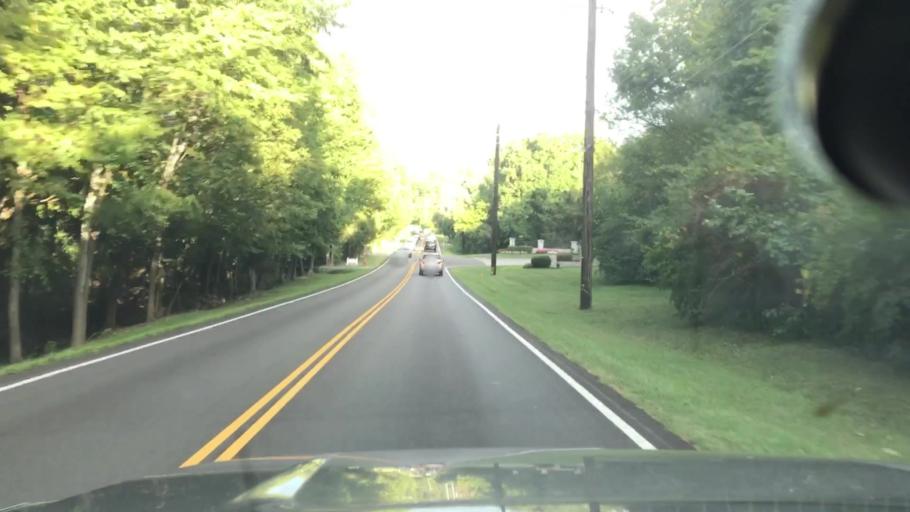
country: US
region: Tennessee
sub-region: Davidson County
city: Forest Hills
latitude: 36.0423
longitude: -86.8259
